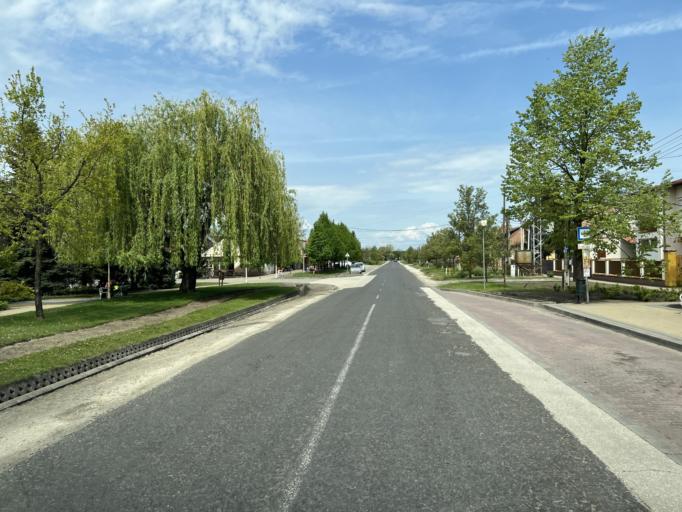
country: HU
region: Pest
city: Csemo
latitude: 47.1160
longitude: 19.6962
